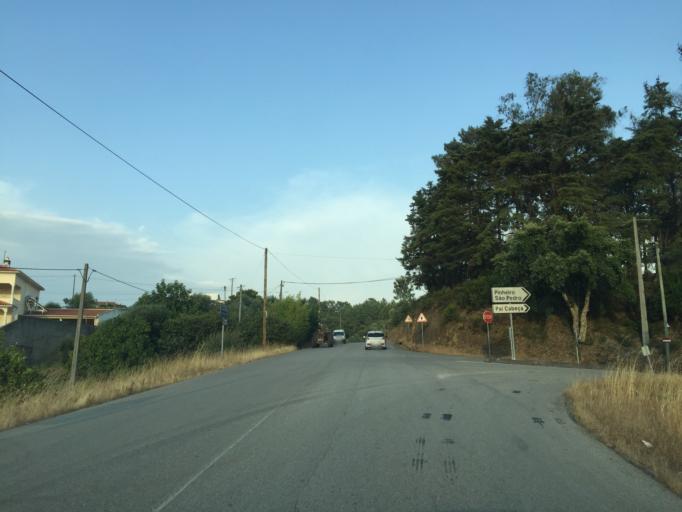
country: PT
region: Santarem
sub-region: Tomar
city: Tomar
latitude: 39.5962
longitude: -8.3304
